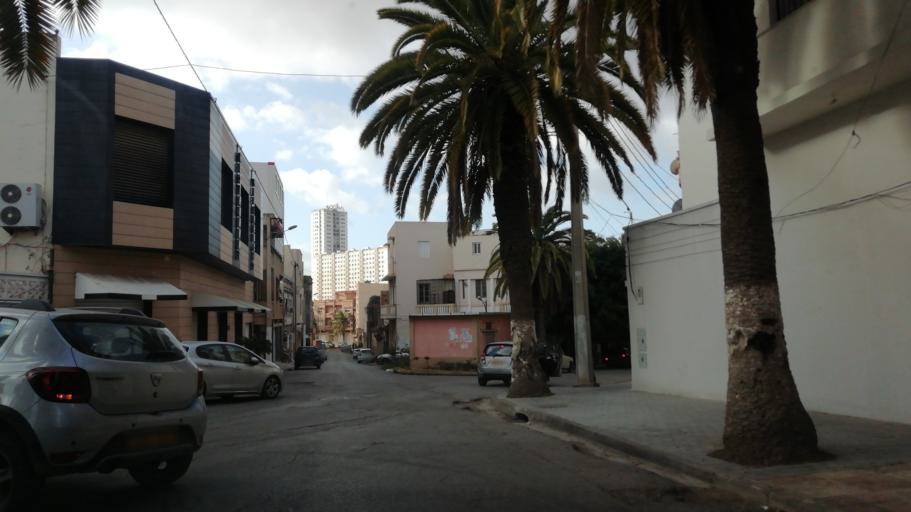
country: DZ
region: Oran
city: Oran
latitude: 35.7111
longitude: -0.6152
